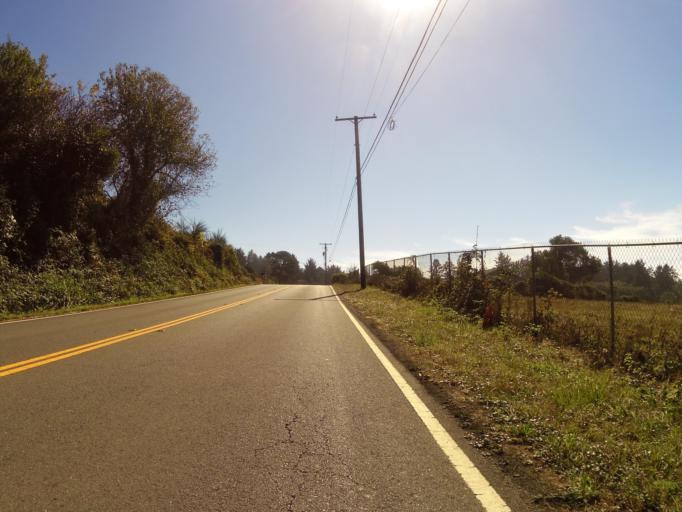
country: US
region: Oregon
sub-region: Curry County
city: Harbor
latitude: 41.9623
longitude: -124.1989
